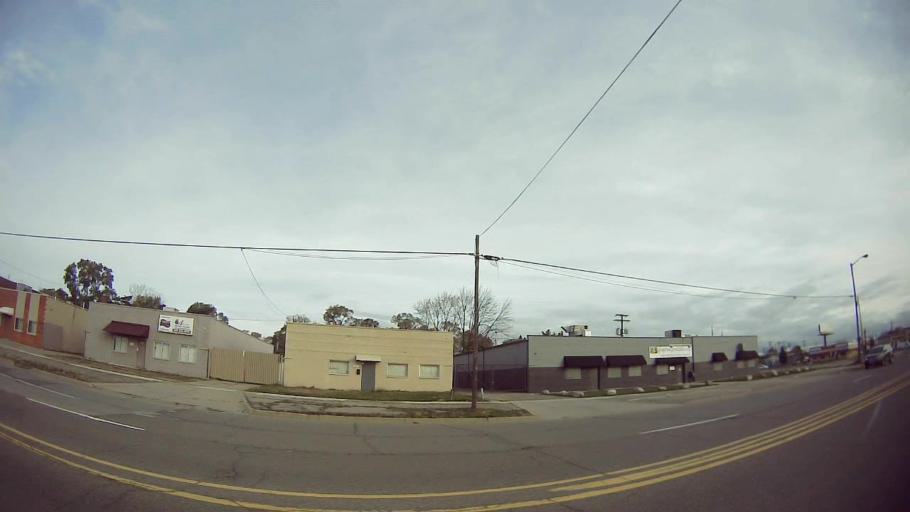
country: US
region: Michigan
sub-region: Oakland County
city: Madison Heights
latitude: 42.4763
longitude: -83.0877
